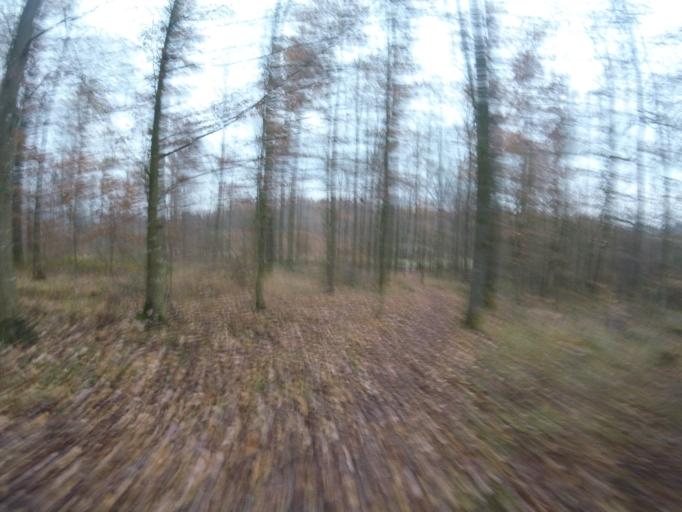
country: DE
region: Baden-Wuerttemberg
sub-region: Regierungsbezirk Stuttgart
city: Oppenweiler
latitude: 48.9826
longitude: 9.4396
